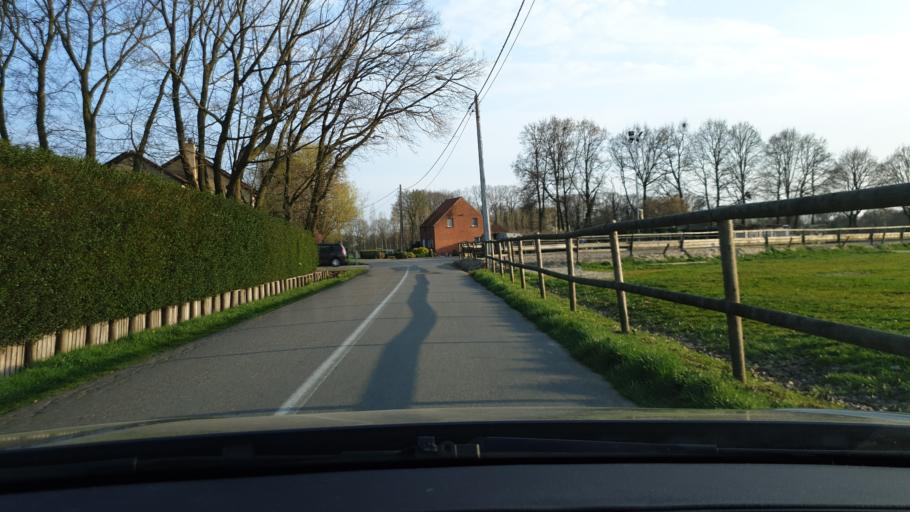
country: BE
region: Flanders
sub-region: Provincie Antwerpen
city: Geel
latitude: 51.1441
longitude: 4.9671
